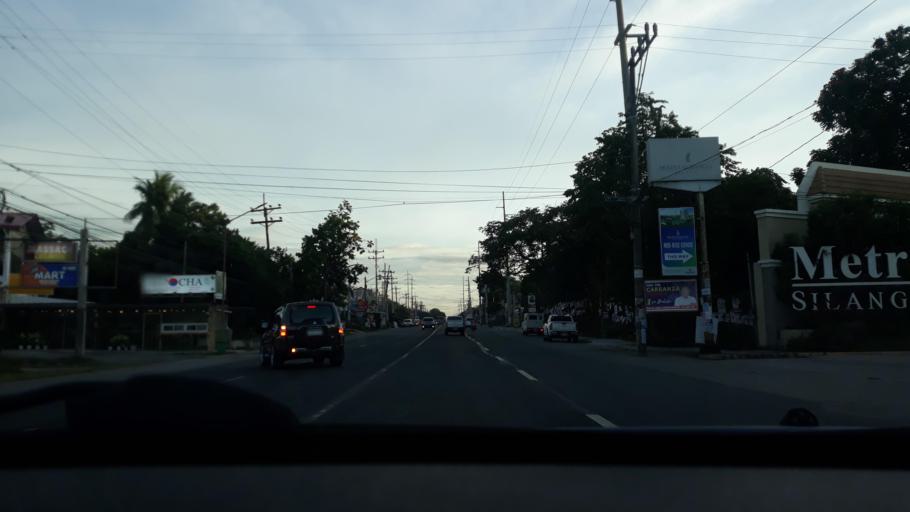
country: PH
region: Calabarzon
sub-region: Province of Cavite
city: Biga
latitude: 14.2405
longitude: 120.9743
